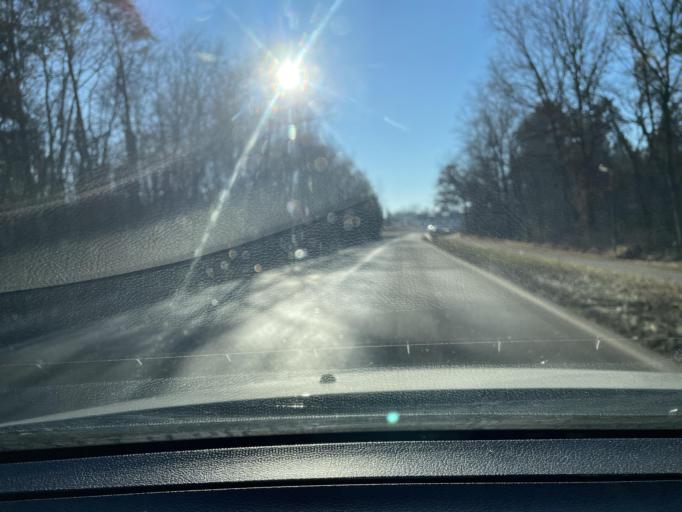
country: DE
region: Bavaria
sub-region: Upper Bavaria
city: Oberschleissheim
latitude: 48.2534
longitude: 11.5813
